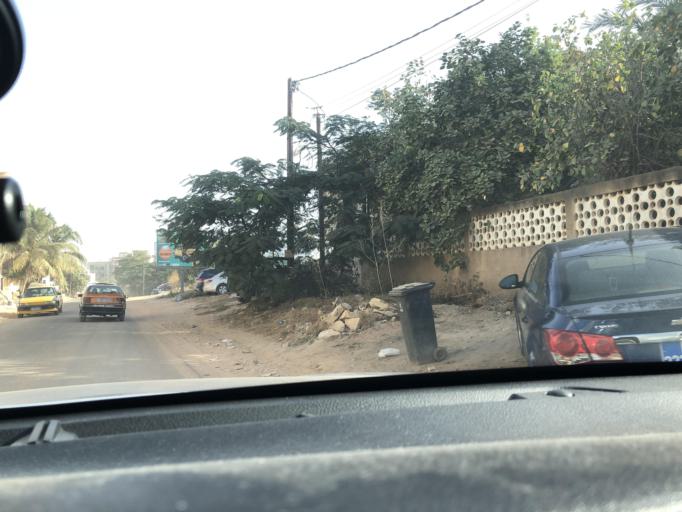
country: SN
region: Dakar
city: Mermoz Boabab
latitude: 14.7311
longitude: -17.4988
